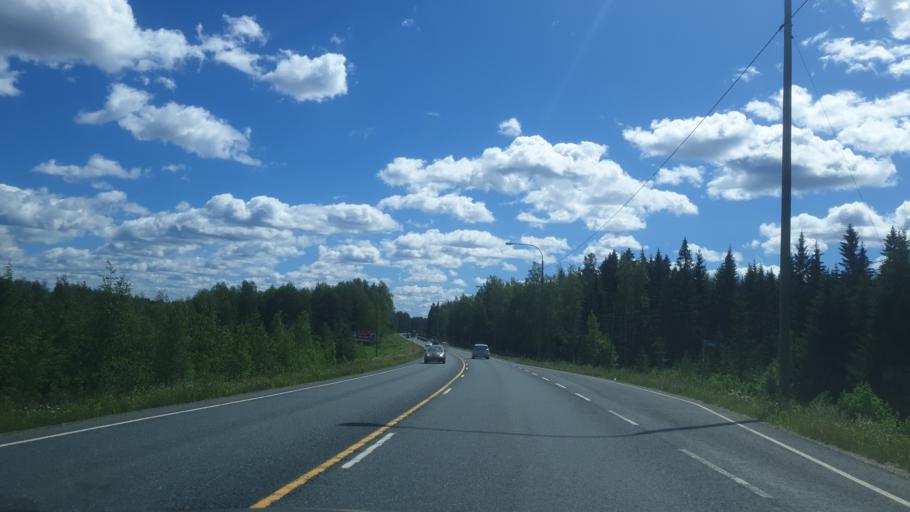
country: FI
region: Northern Savo
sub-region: Varkaus
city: Leppaevirta
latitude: 62.5403
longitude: 27.6338
